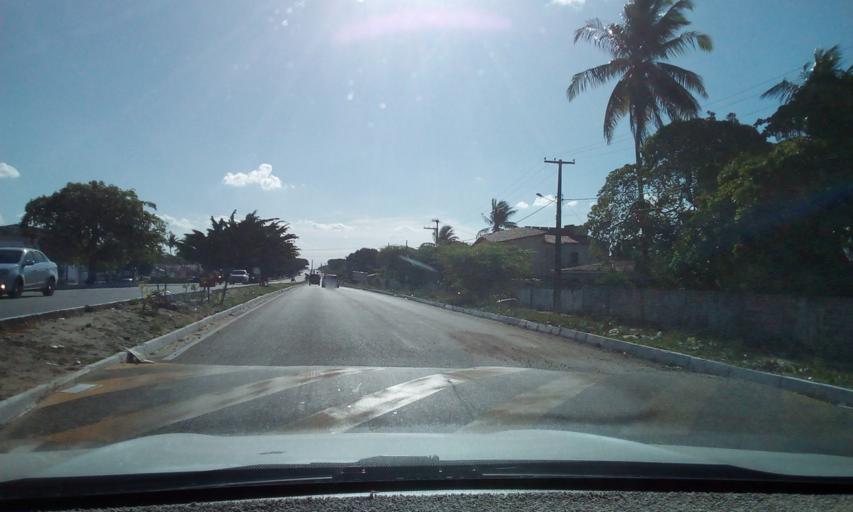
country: BR
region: Paraiba
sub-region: Bayeux
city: Bayeux
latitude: -7.1352
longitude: -34.9388
